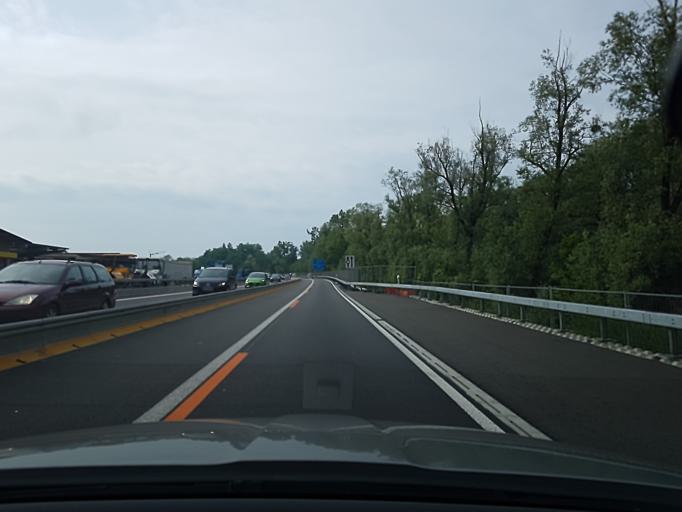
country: CH
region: Saint Gallen
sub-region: Wahlkreis Rheintal
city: Rheineck
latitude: 47.4760
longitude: 9.5861
